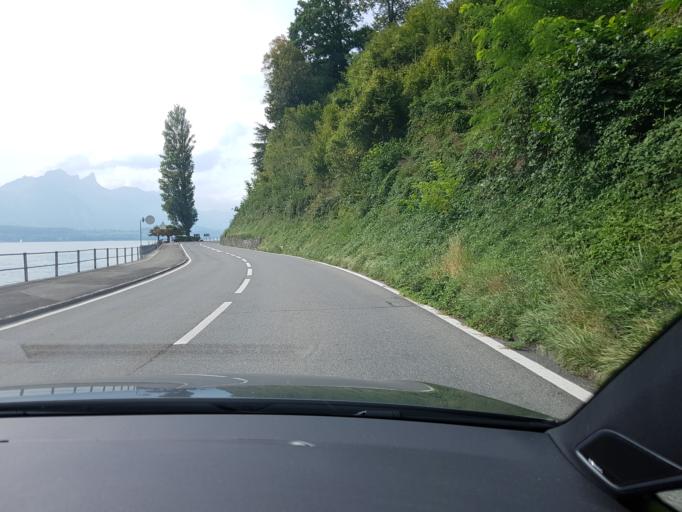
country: CH
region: Bern
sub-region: Thun District
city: Sigriswil
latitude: 46.7083
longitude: 7.7223
